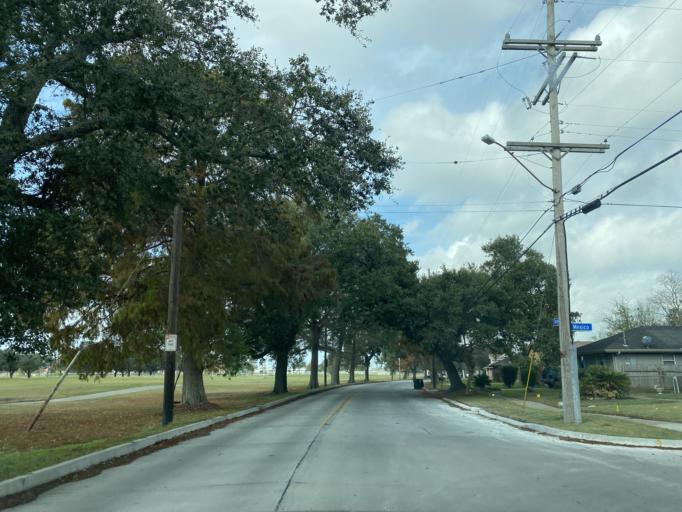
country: US
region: Louisiana
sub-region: Saint Bernard Parish
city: Arabi
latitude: 30.0239
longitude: -90.0384
